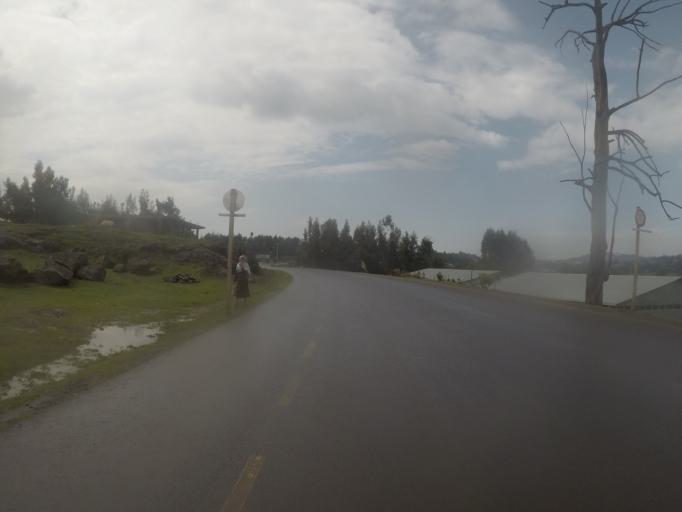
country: ET
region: Amhara
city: Debark'
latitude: 13.1394
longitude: 37.8943
